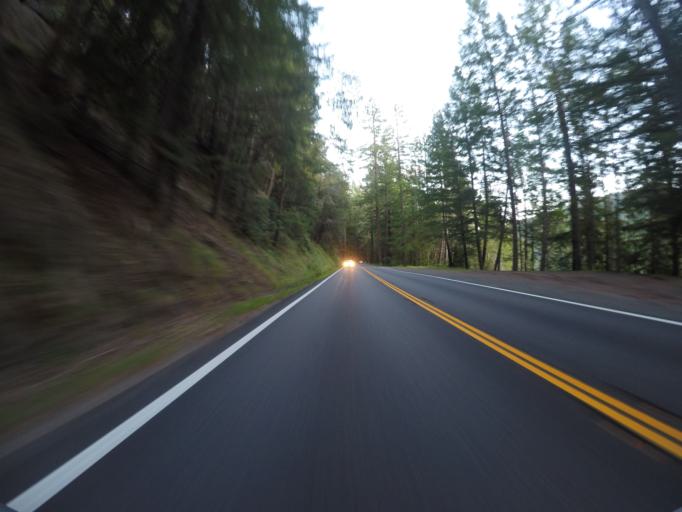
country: US
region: California
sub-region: Humboldt County
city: Redway
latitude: 39.9128
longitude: -123.7586
